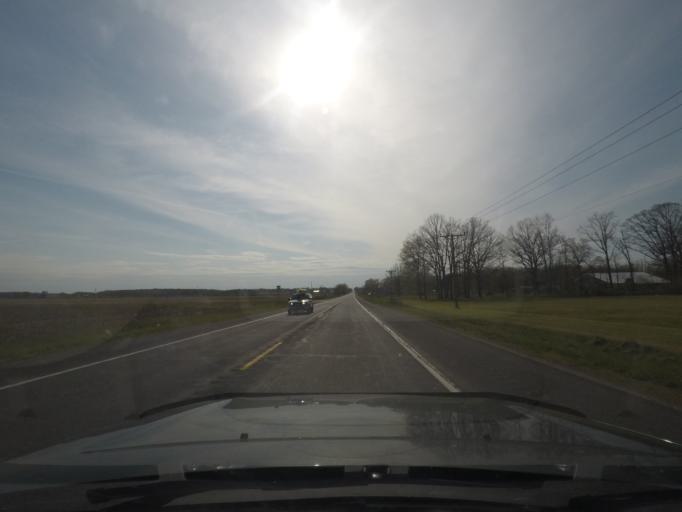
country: US
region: Michigan
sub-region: Berrien County
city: Three Oaks
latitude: 41.7988
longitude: -86.5800
